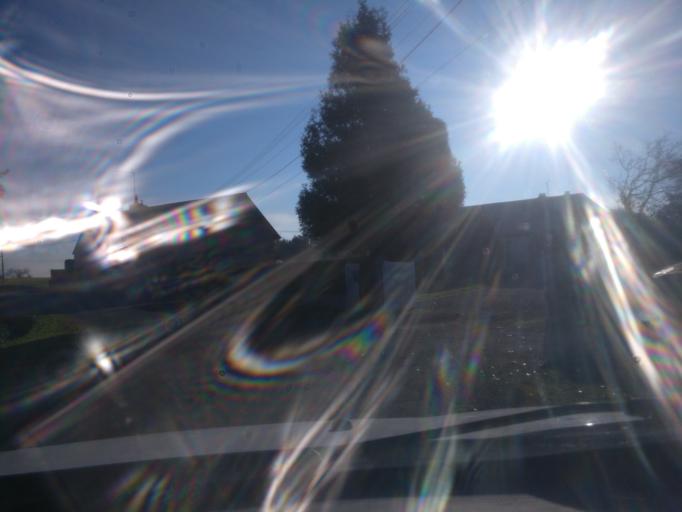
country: FR
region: Brittany
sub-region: Departement d'Ille-et-Vilaine
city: Chavagne
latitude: 48.0120
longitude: -1.7932
